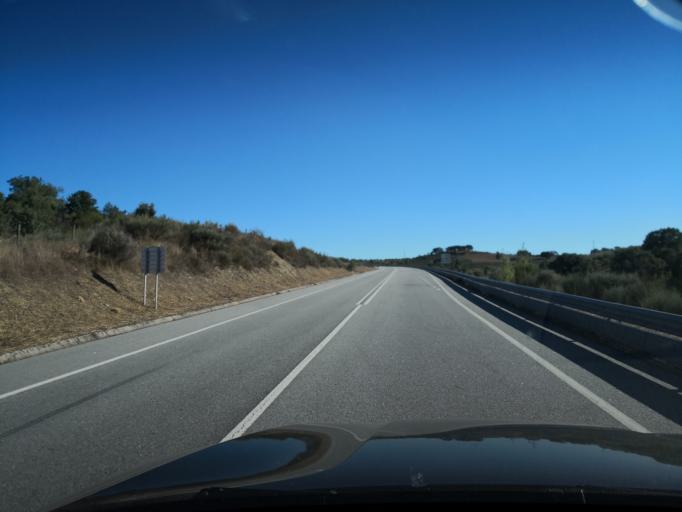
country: PT
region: Braganca
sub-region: Mirandela
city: Mirandela
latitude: 41.4994
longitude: -7.2303
